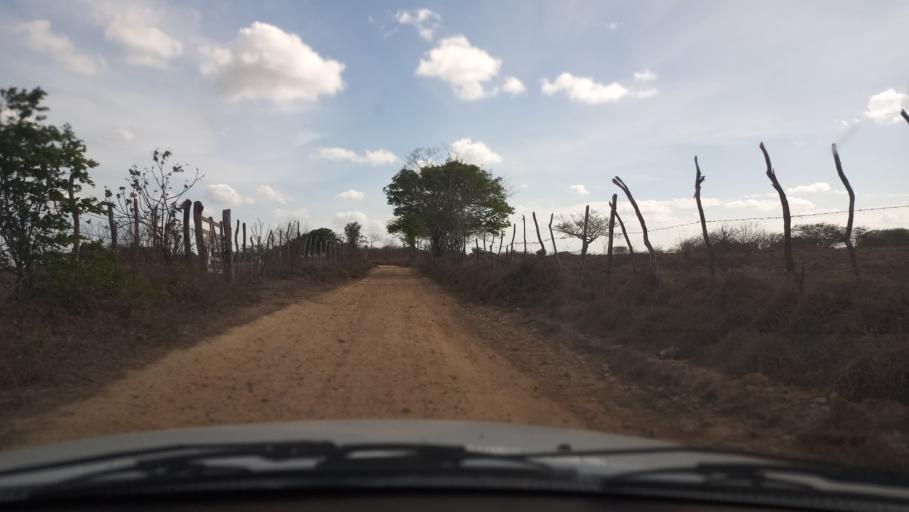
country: BR
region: Rio Grande do Norte
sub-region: Goianinha
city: Goianinha
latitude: -6.3150
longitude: -35.3074
